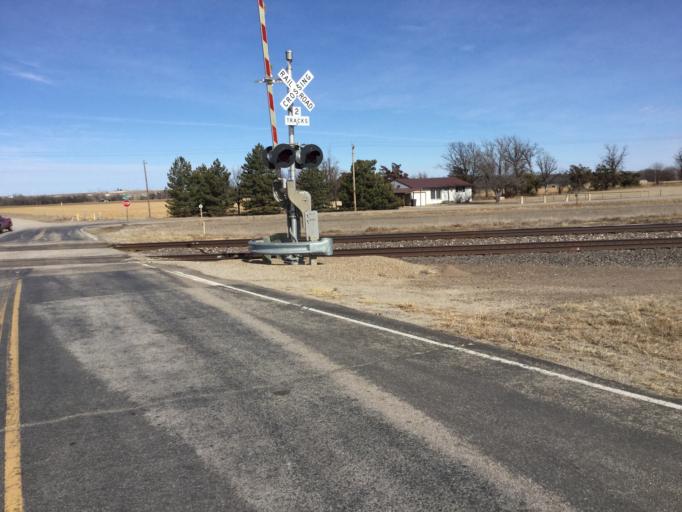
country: US
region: Kansas
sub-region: Ellis County
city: Hays
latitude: 38.8914
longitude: -99.3732
